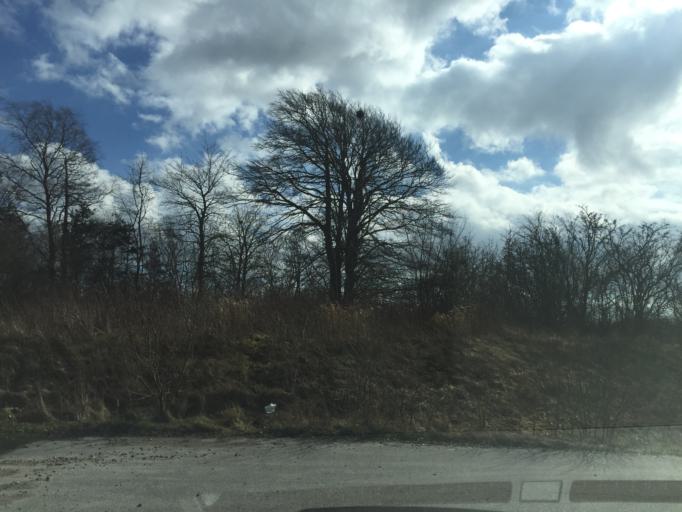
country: DK
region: South Denmark
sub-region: Svendborg Kommune
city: Svendborg
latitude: 55.1129
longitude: 10.5583
